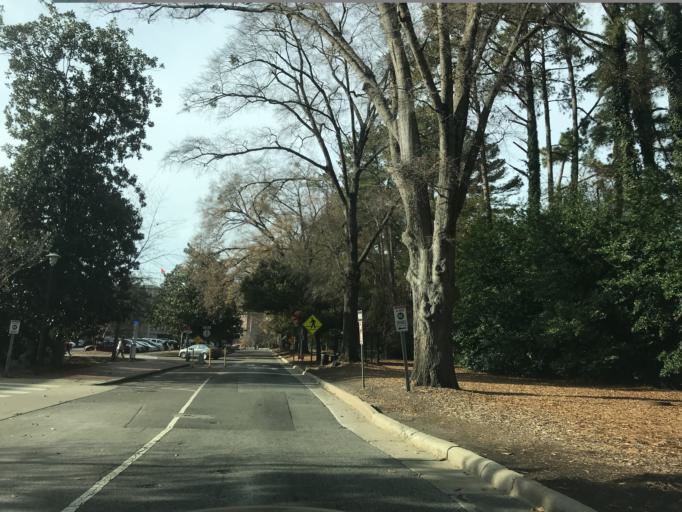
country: US
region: North Carolina
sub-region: Wake County
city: West Raleigh
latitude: 35.7837
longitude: -78.6677
